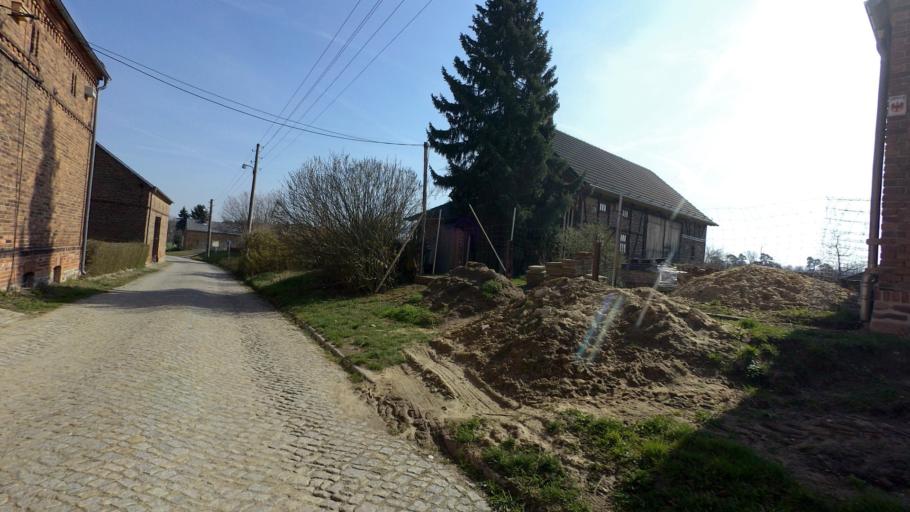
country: DE
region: Brandenburg
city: Golssen
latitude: 51.9831
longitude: 13.5428
